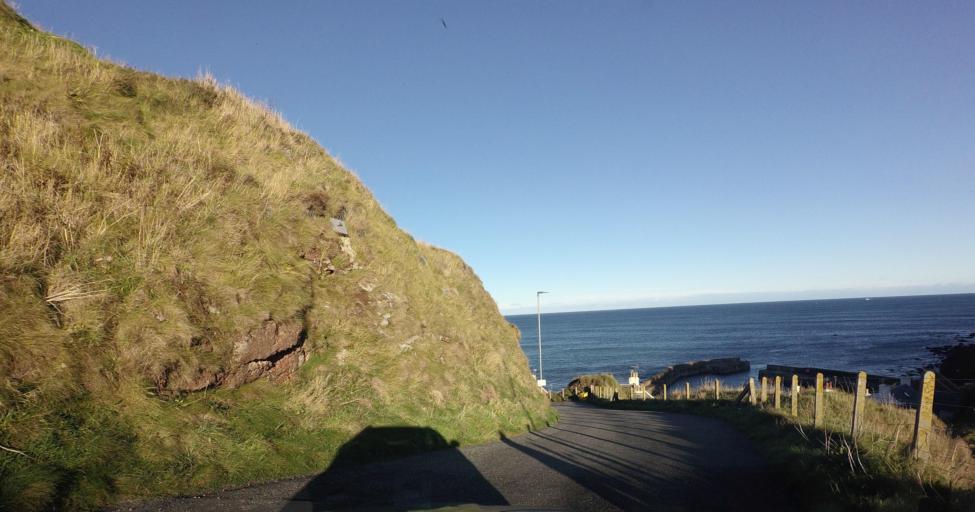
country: GB
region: Scotland
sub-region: Aberdeenshire
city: Rosehearty
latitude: 57.6783
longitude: -2.2588
